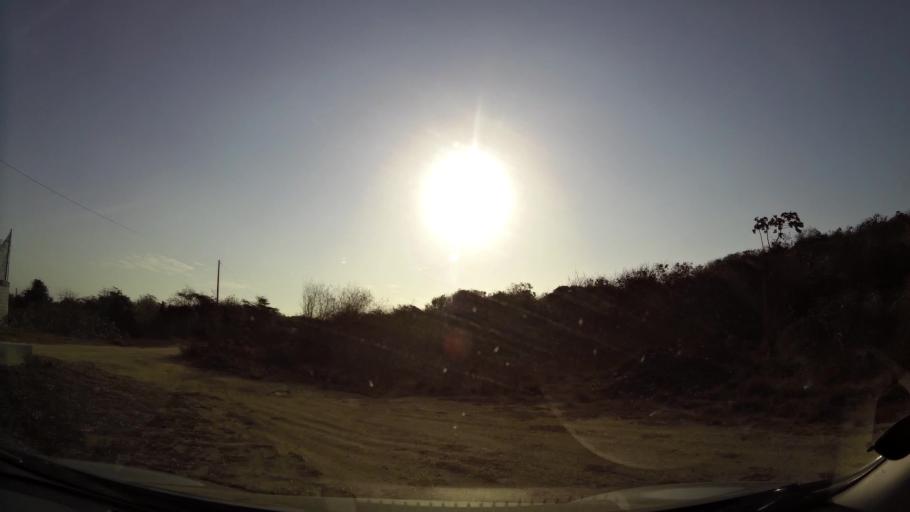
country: CO
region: Atlantico
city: Barranquilla
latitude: 11.0305
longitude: -74.8272
